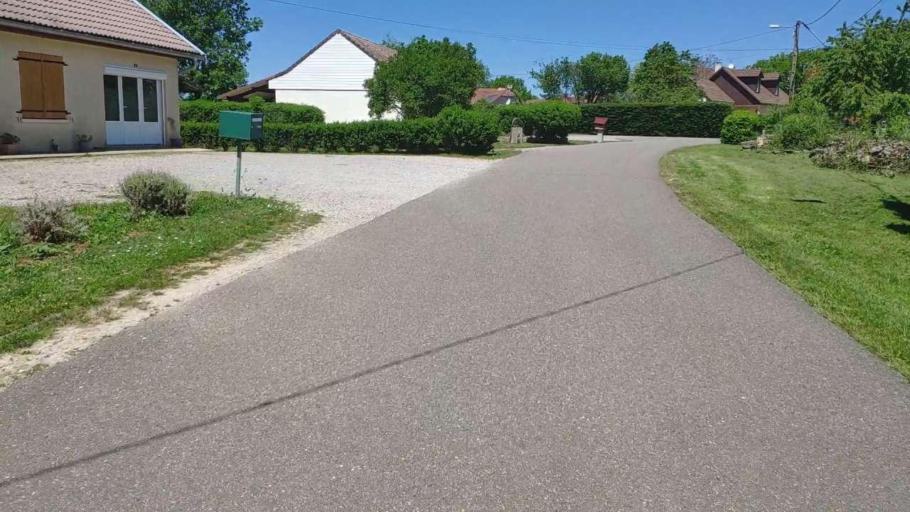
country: FR
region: Franche-Comte
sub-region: Departement du Jura
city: Poligny
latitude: 46.7340
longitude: 5.6909
